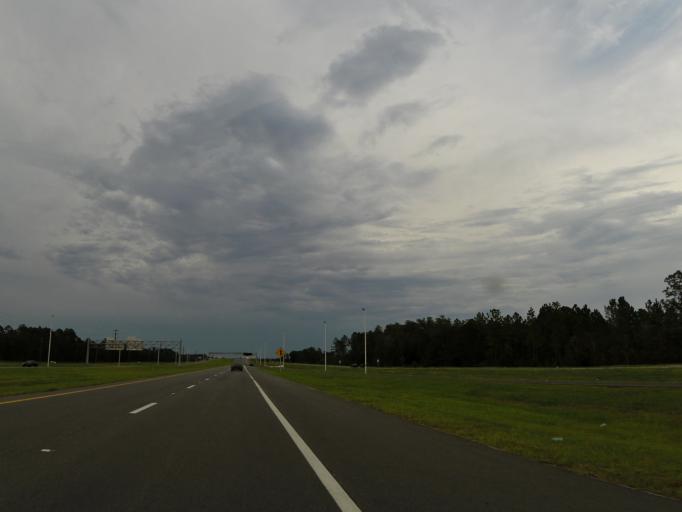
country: US
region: Florida
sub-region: Clay County
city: Lakeside
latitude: 30.1237
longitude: -81.8303
